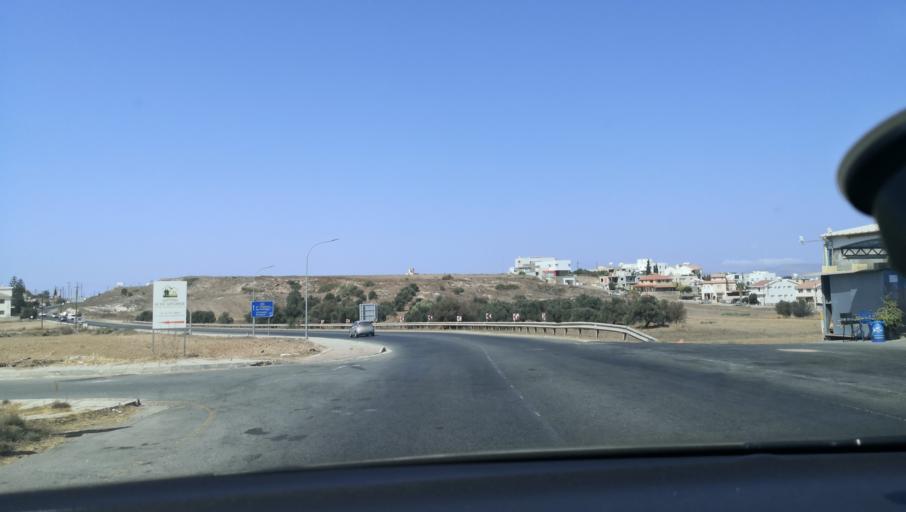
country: CY
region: Lefkosia
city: Kato Deftera
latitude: 35.1153
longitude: 33.2836
